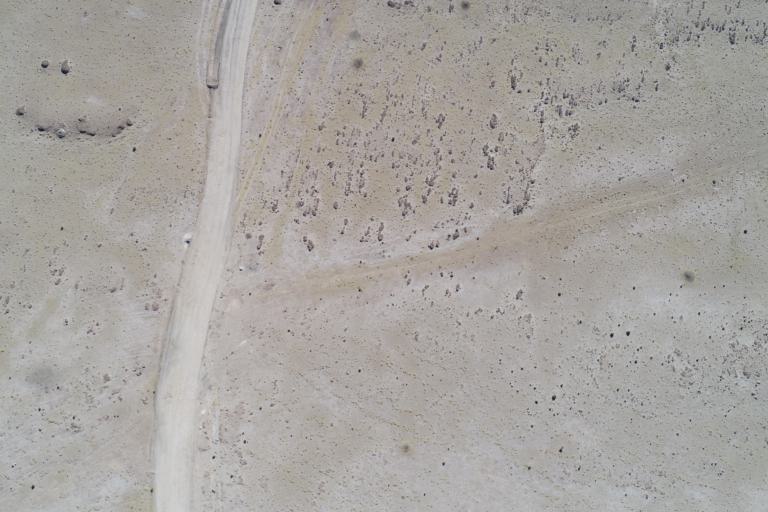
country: BO
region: Potosi
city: Colchani
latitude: -20.3525
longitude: -66.9016
